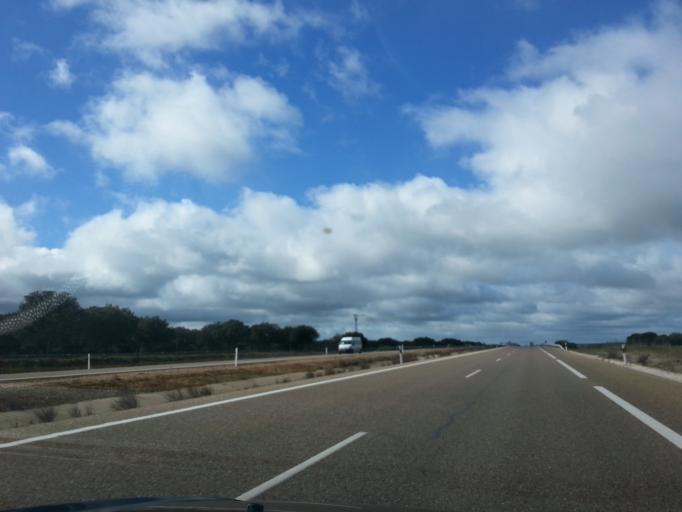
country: ES
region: Castille and Leon
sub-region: Provincia de Salamanca
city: Aldehuela de la Boveda
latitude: 40.8611
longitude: -6.0207
